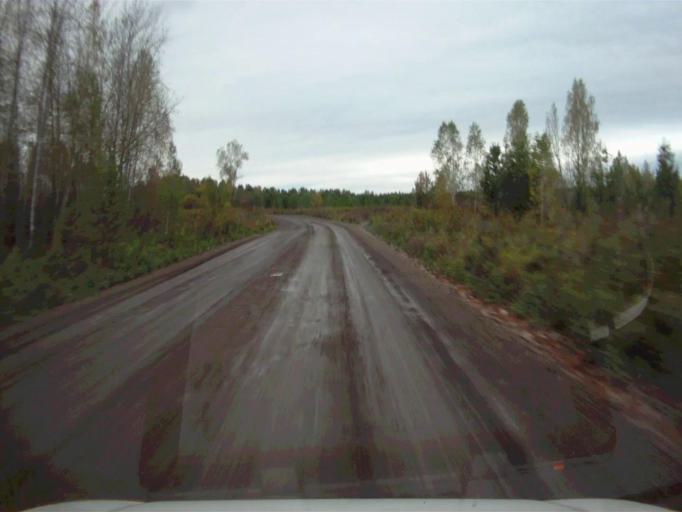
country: RU
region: Chelyabinsk
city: Nyazepetrovsk
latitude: 56.1384
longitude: 59.2992
